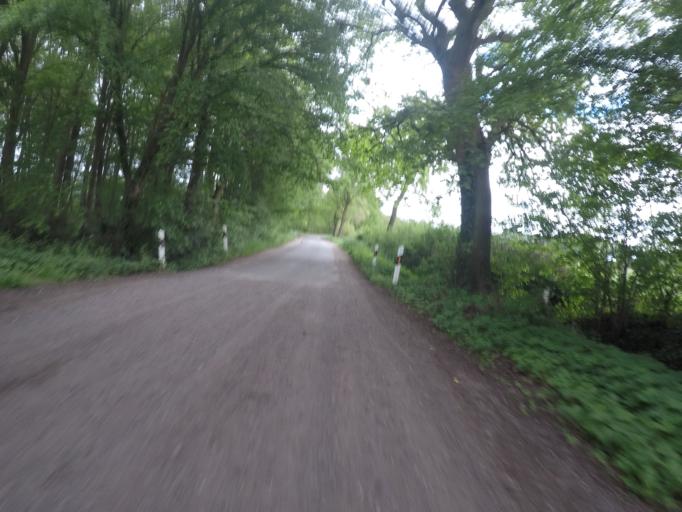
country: DE
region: Schleswig-Holstein
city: Quickborn
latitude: 53.7102
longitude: 9.9178
